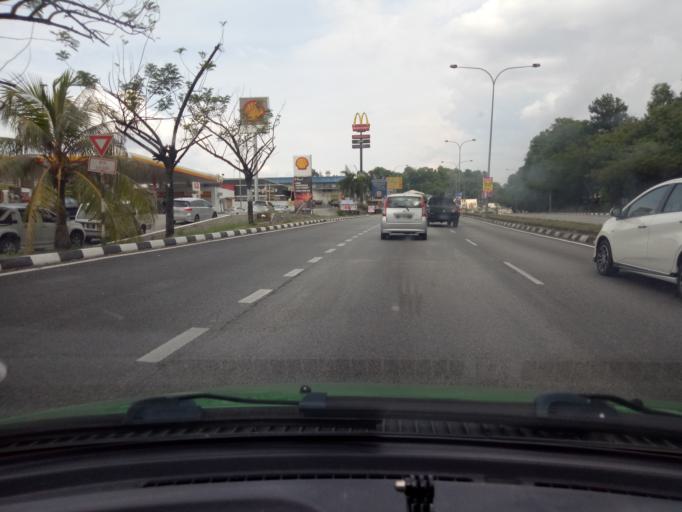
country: MY
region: Selangor
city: Kampong Baharu Balakong
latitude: 3.0078
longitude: 101.8034
